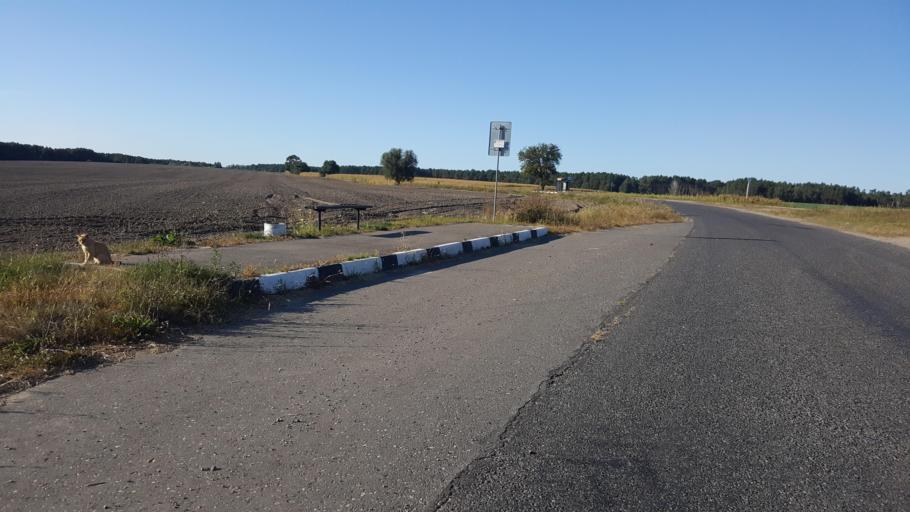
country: BY
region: Brest
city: Vysokaye
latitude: 52.3415
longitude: 23.2894
